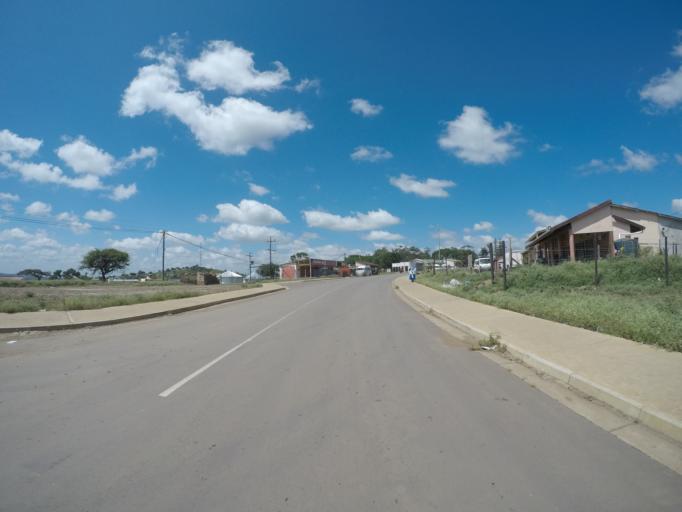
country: ZA
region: KwaZulu-Natal
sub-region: uThungulu District Municipality
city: Empangeni
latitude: -28.6052
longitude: 31.7437
